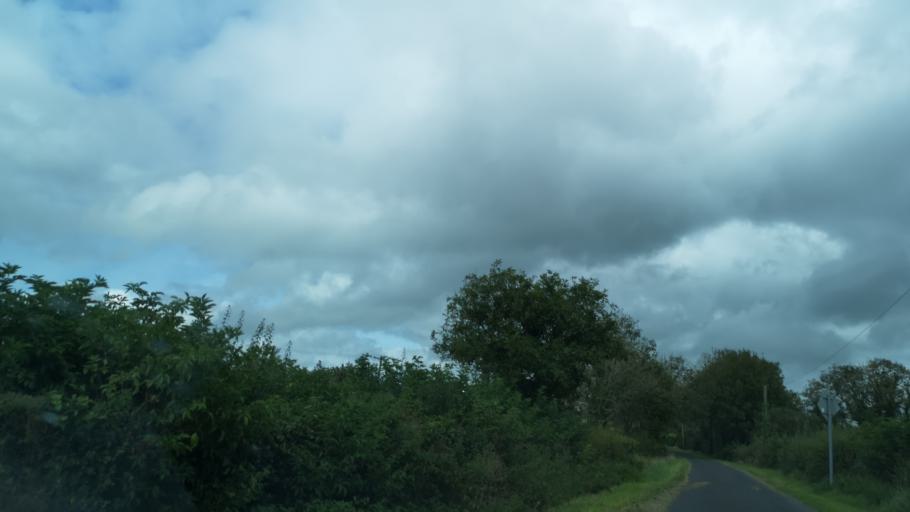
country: IE
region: Connaught
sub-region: County Galway
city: Athenry
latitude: 53.2898
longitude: -8.6641
